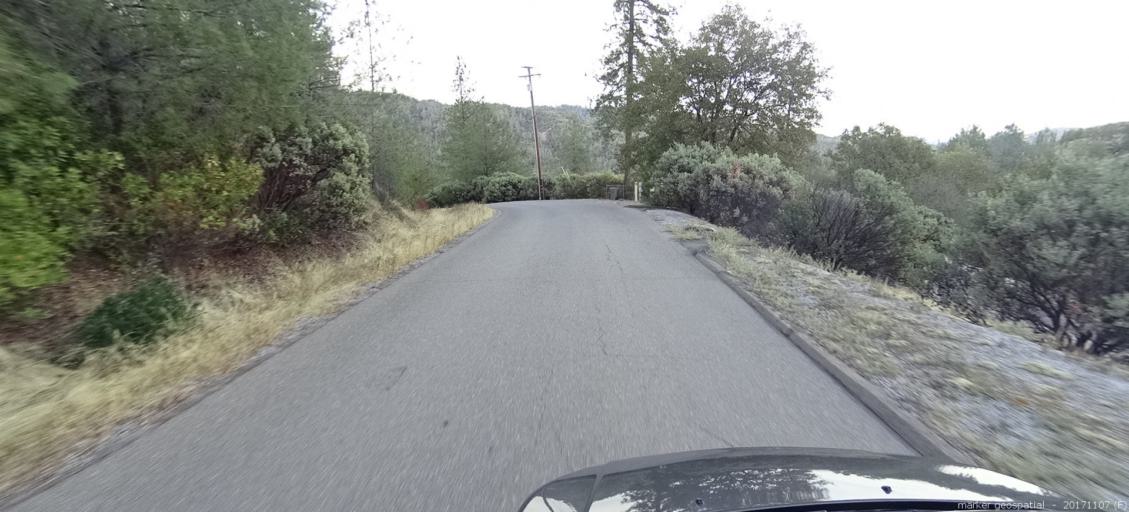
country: US
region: California
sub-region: Shasta County
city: Shasta
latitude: 40.5429
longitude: -122.5008
